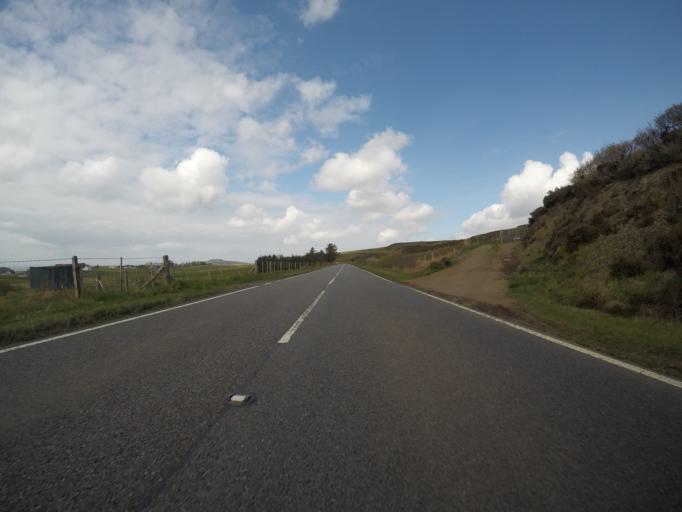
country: GB
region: Scotland
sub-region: Highland
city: Portree
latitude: 57.5573
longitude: -6.3638
